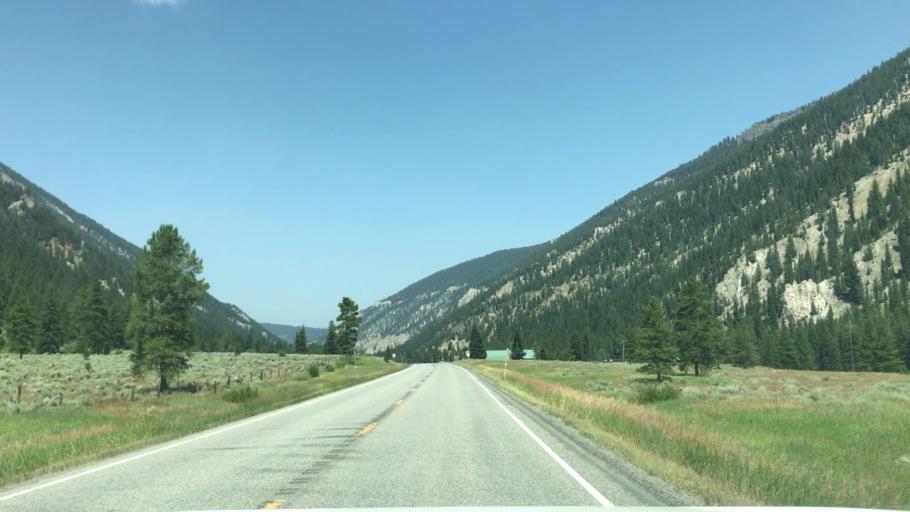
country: US
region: Montana
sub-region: Gallatin County
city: Big Sky
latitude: 45.1124
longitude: -111.2243
